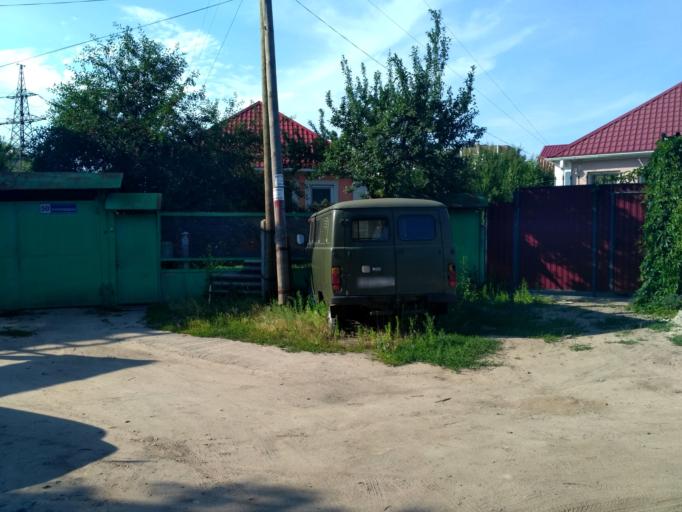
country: RU
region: Voronezj
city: Voronezh
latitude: 51.6760
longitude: 39.1334
